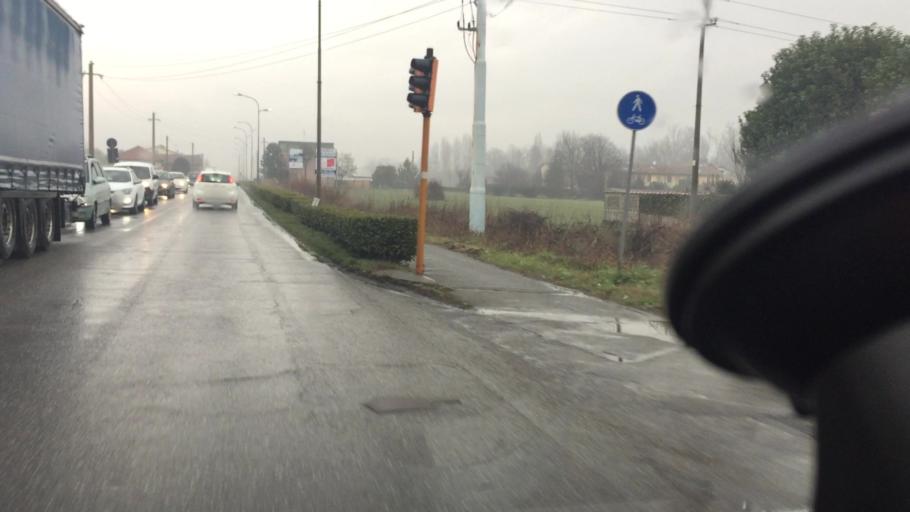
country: IT
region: Lombardy
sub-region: Citta metropolitana di Milano
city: Vaprio d'Adda
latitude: 45.5858
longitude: 9.5217
